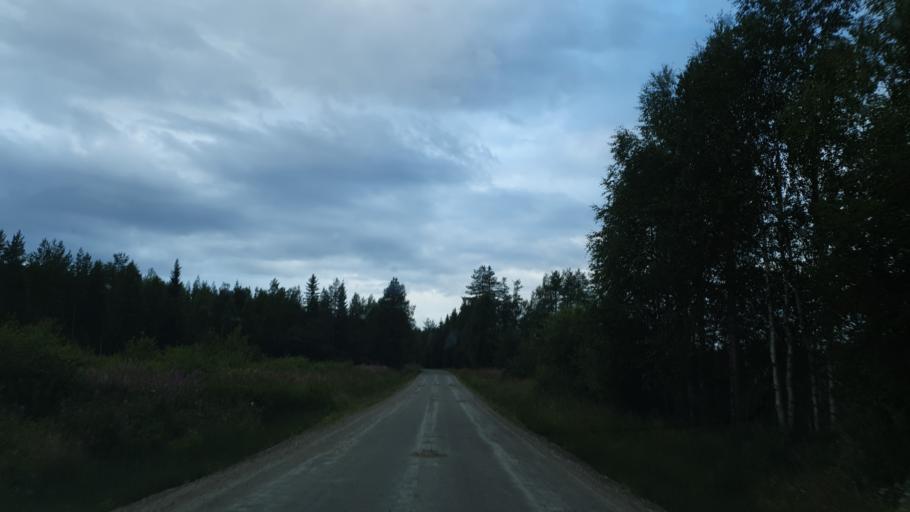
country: FI
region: Kainuu
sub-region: Kehys-Kainuu
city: Kuhmo
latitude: 64.2012
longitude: 29.3696
